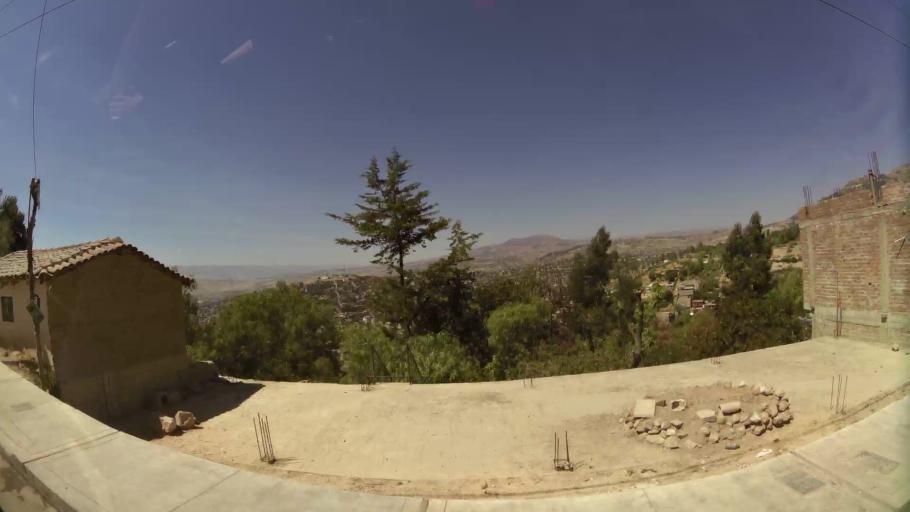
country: PE
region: Ayacucho
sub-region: Provincia de Huamanga
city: Ayacucho
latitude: -13.1665
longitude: -74.2354
